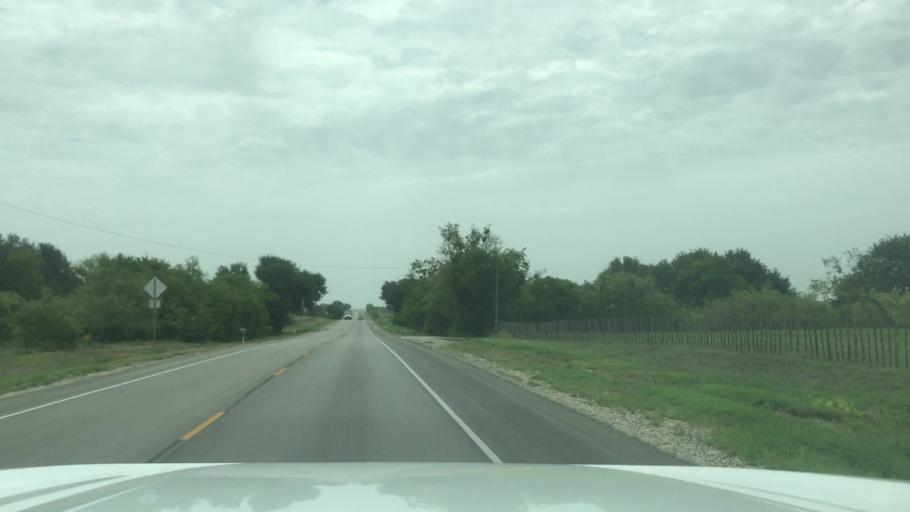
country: US
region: Texas
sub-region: Erath County
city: Dublin
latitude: 32.0846
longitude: -98.2519
